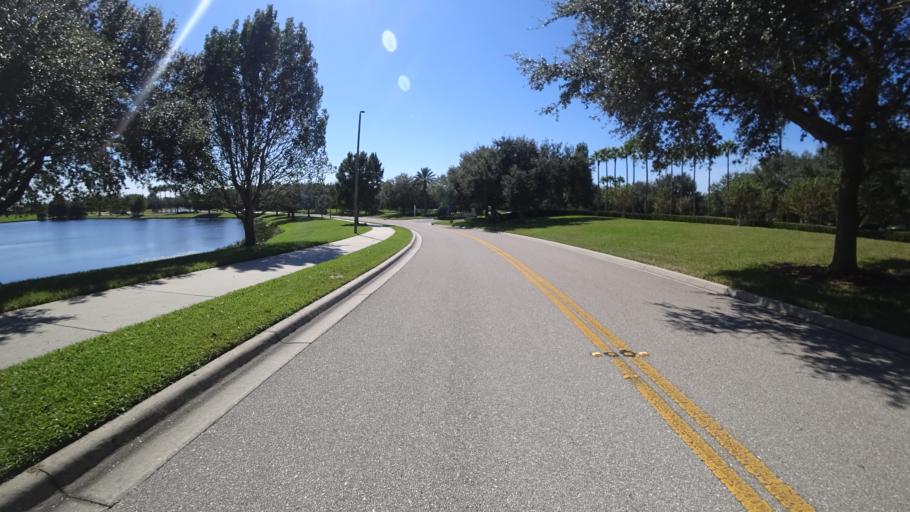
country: US
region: Florida
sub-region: Sarasota County
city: The Meadows
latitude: 27.4032
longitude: -82.4111
